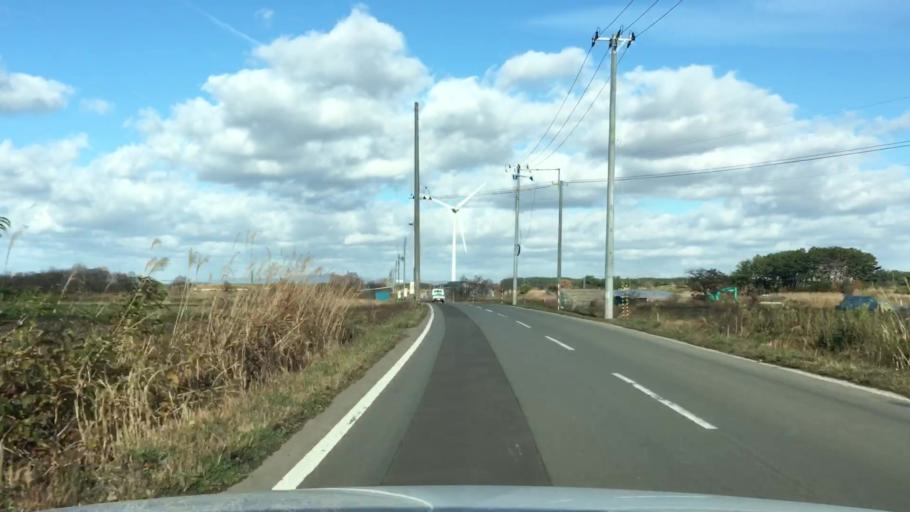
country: JP
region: Aomori
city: Shimokizukuri
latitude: 40.8564
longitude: 140.3029
